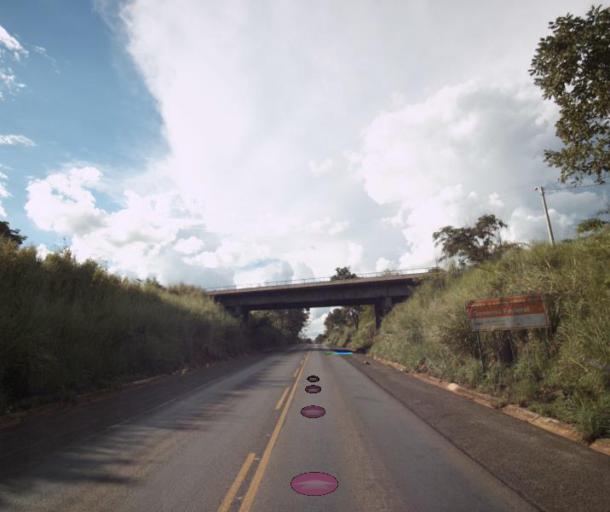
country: BR
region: Goias
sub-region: Rialma
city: Rialma
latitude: -15.3204
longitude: -49.5720
